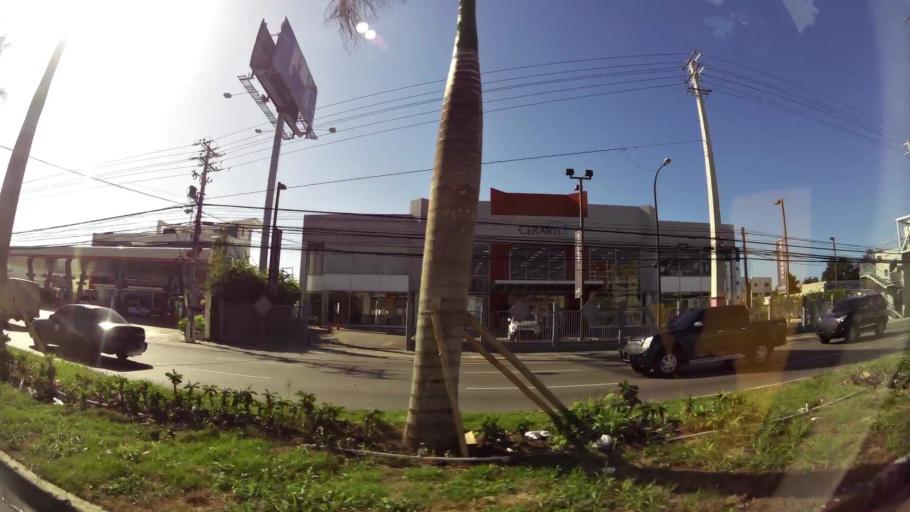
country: DO
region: Nacional
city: Bella Vista
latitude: 18.4586
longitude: -69.9452
